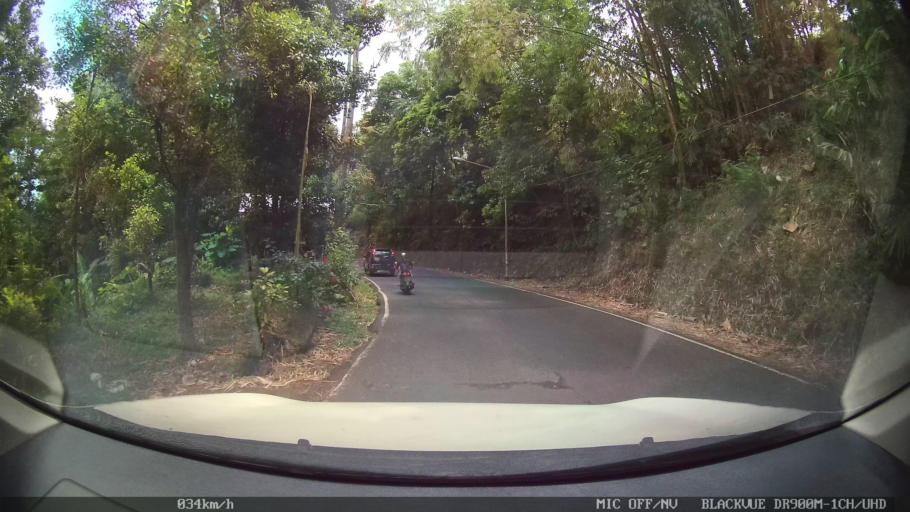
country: ID
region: Bali
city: Banjar Ambengan
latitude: -8.1873
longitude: 115.1354
